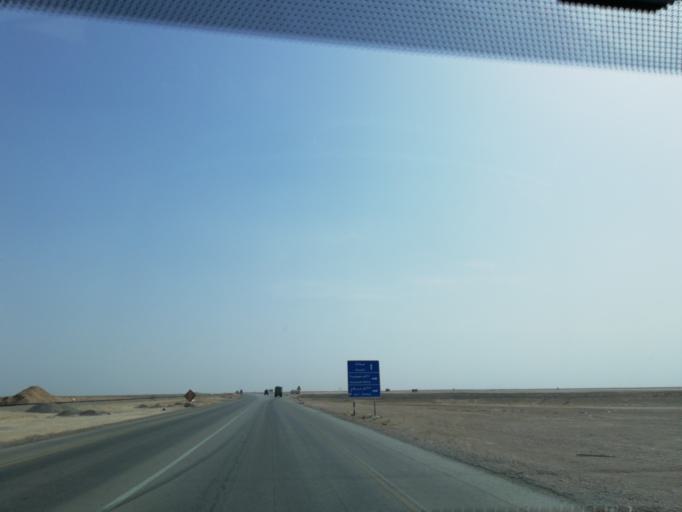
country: OM
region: Muhafazat ad Dakhiliyah
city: Adam
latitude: 21.6422
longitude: 57.3064
